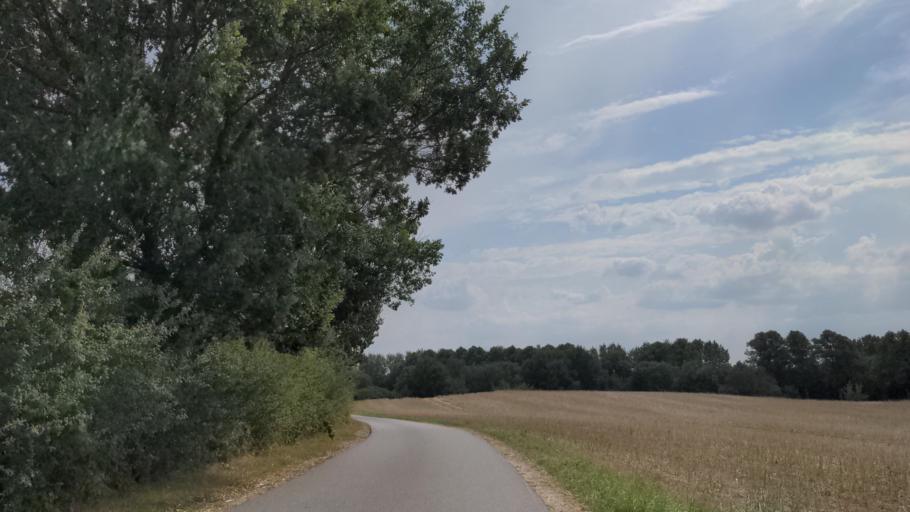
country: DE
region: Mecklenburg-Vorpommern
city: Selmsdorf
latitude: 53.8718
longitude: 10.8961
